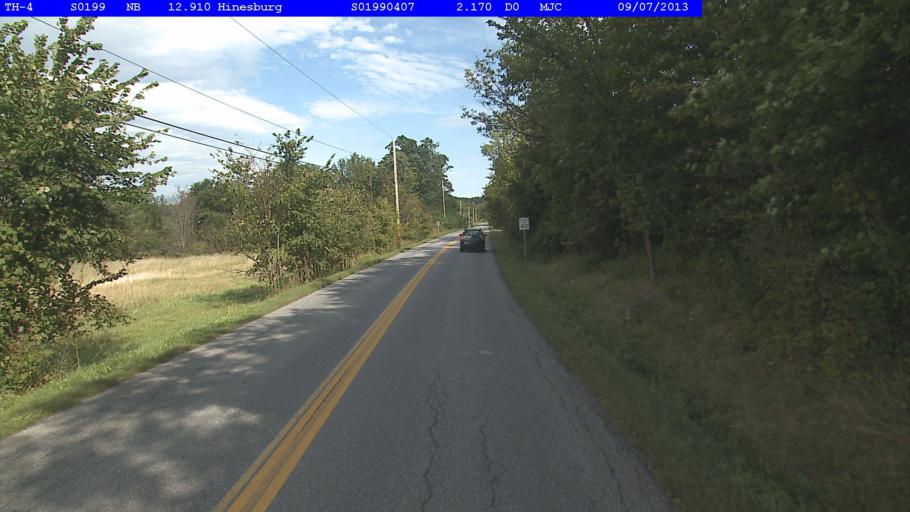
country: US
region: Vermont
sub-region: Chittenden County
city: Hinesburg
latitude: 44.3091
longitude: -73.1093
